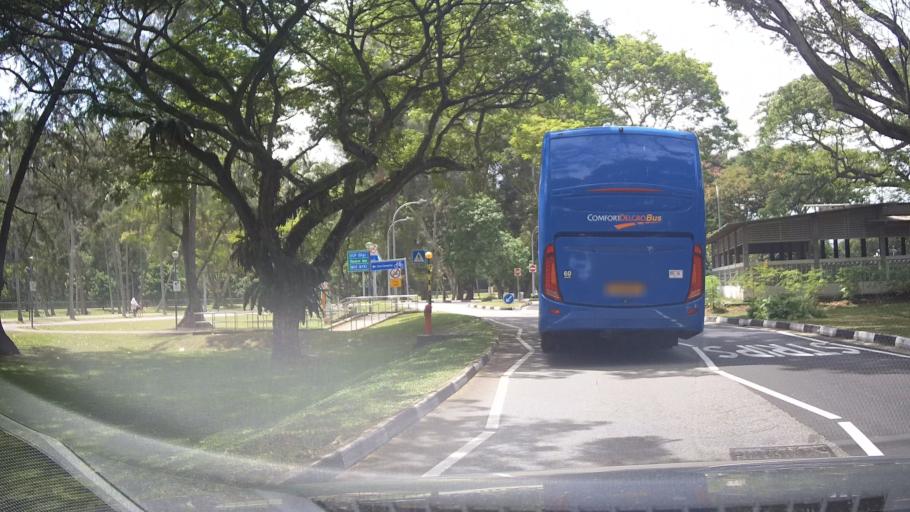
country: SG
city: Singapore
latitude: 1.2955
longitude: 103.8948
